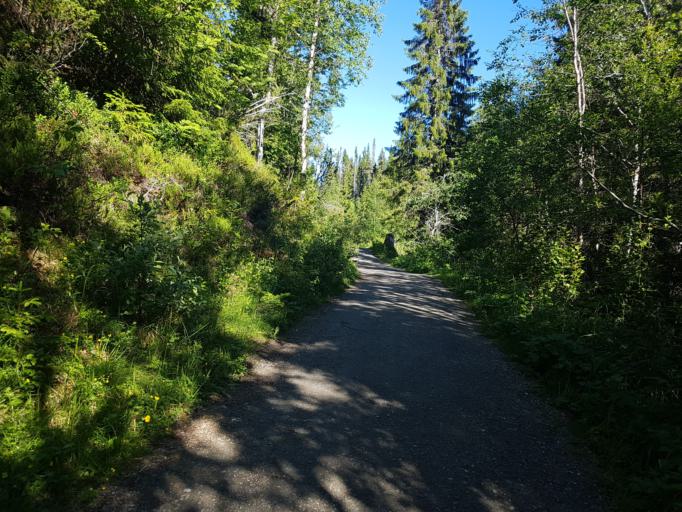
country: NO
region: Sor-Trondelag
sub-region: Trondheim
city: Trondheim
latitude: 63.4220
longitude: 10.2939
